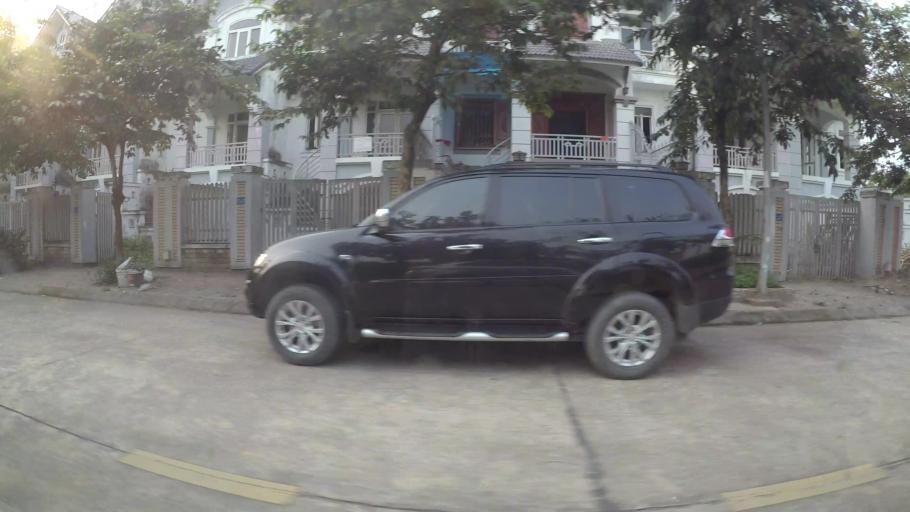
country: VN
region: Ha Noi
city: Cau Dien
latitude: 21.0046
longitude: 105.7340
